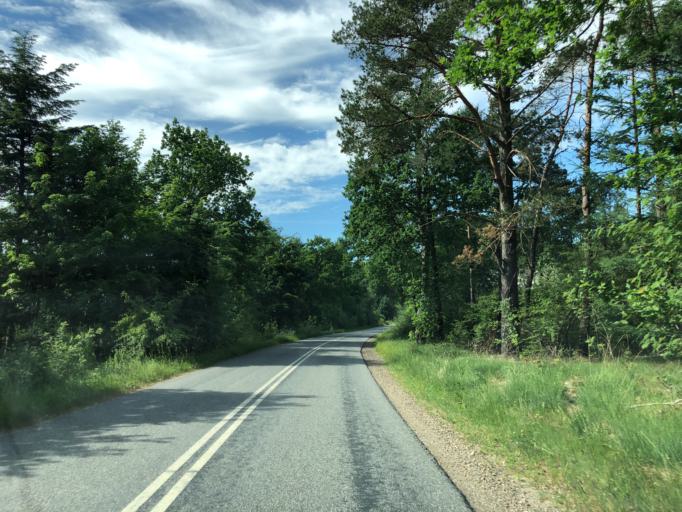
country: DK
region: Central Jutland
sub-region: Herning Kommune
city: Lind
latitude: 56.0351
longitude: 8.9408
